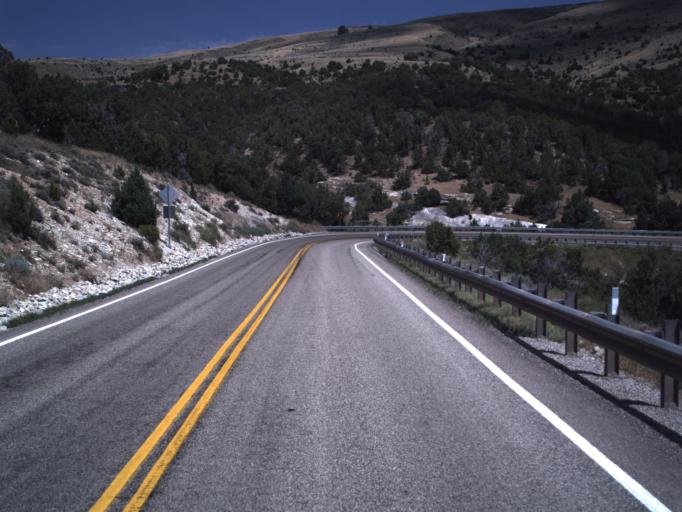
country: US
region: Utah
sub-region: Uintah County
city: Vernal
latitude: 40.6428
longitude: -109.4855
